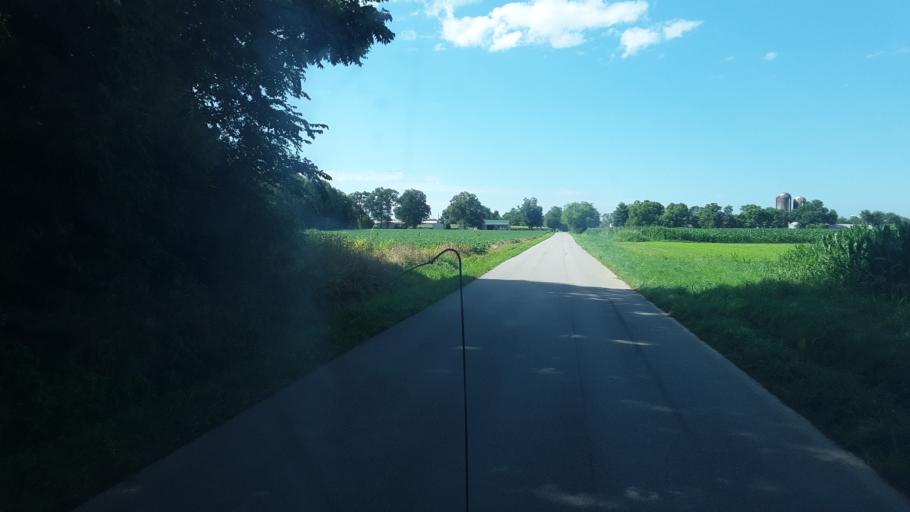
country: US
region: Kentucky
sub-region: Todd County
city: Guthrie
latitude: 36.7294
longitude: -87.1680
